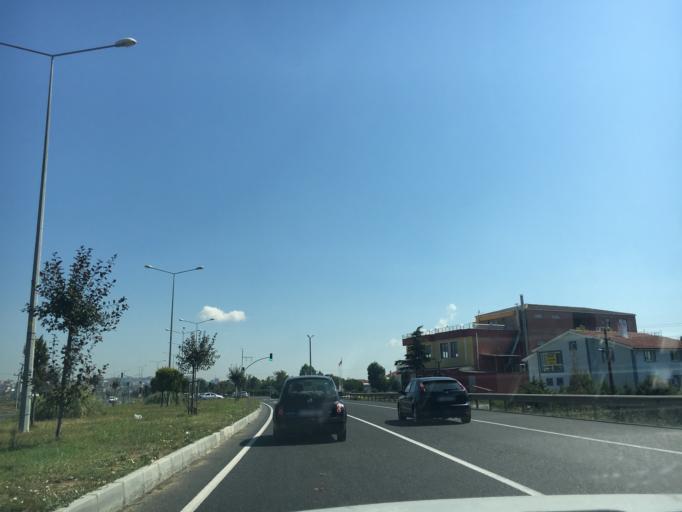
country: TR
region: Tekirdag
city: Sultankoy
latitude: 41.0078
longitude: 27.9798
